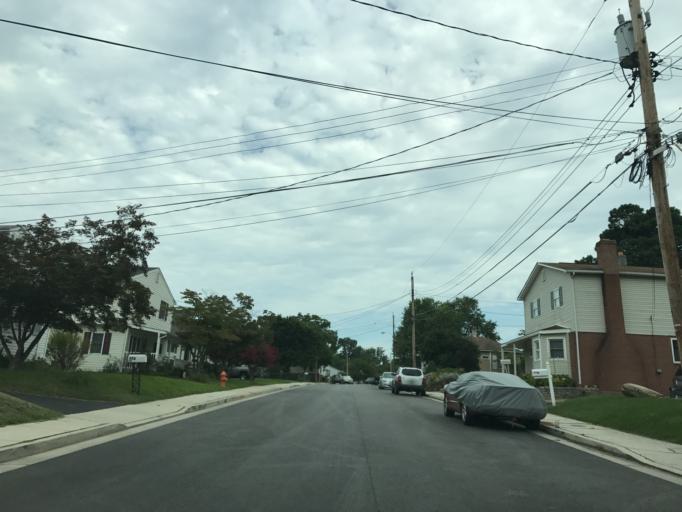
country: US
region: Maryland
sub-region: Baltimore County
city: Essex
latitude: 39.3203
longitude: -76.4813
